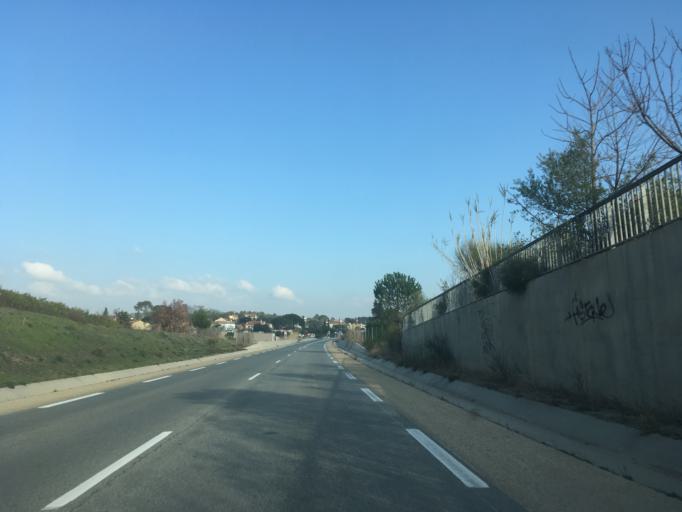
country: FR
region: Provence-Alpes-Cote d'Azur
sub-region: Departement du Var
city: Vidauban
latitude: 43.4280
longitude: 6.4355
